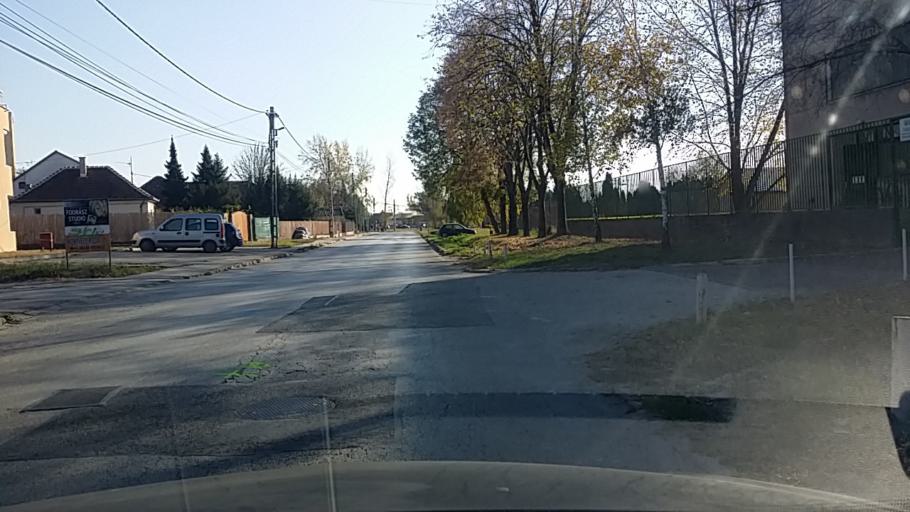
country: HU
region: Pest
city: Szigetszentmiklos
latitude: 47.3400
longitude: 19.0289
